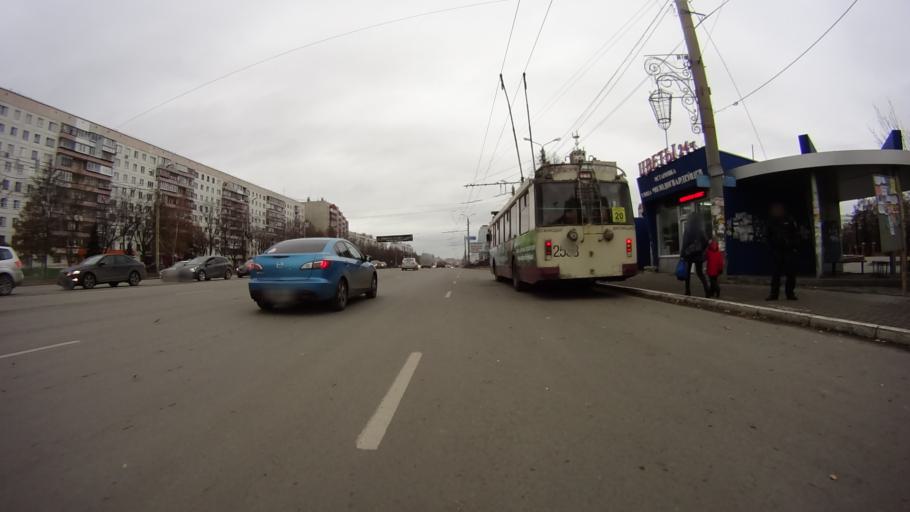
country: RU
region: Chelyabinsk
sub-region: Gorod Chelyabinsk
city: Chelyabinsk
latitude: 55.1942
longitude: 61.3324
